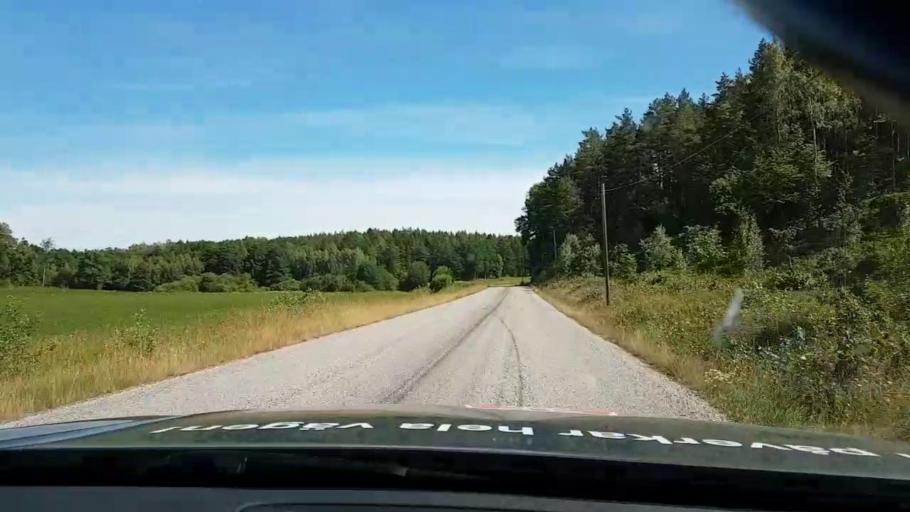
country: SE
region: Kalmar
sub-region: Vasterviks Kommun
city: Forserum
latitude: 57.9180
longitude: 16.6224
